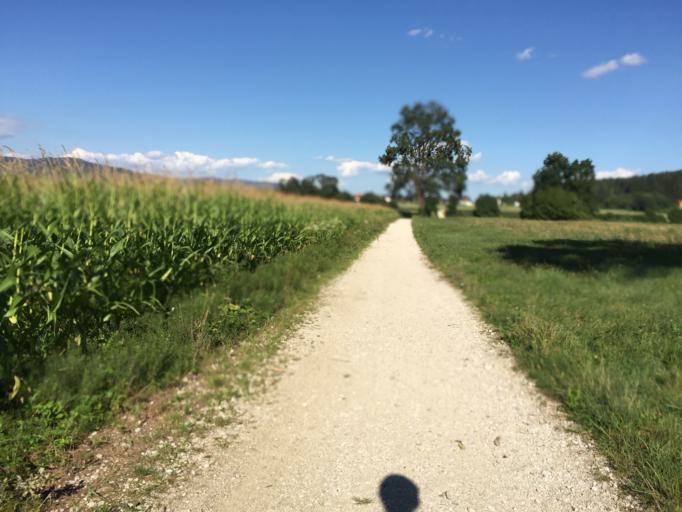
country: AT
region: Carinthia
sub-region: Politischer Bezirk Volkermarkt
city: Feistritz ob Bleiburg
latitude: 46.5588
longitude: 14.7545
